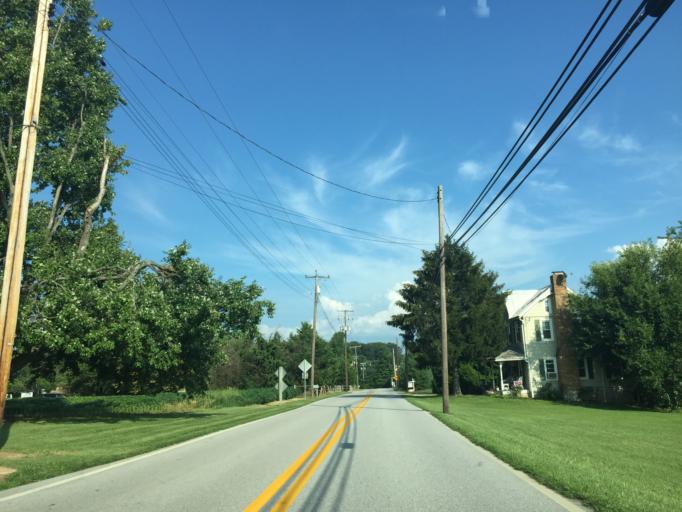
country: US
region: Maryland
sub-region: Carroll County
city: Manchester
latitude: 39.6509
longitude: -76.8629
